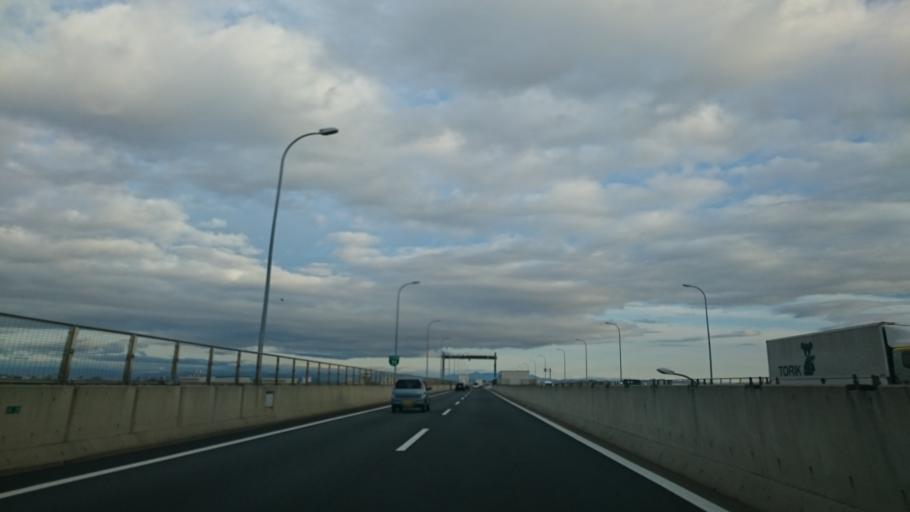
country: JP
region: Aichi
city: Komaki
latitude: 35.2415
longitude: 136.9088
